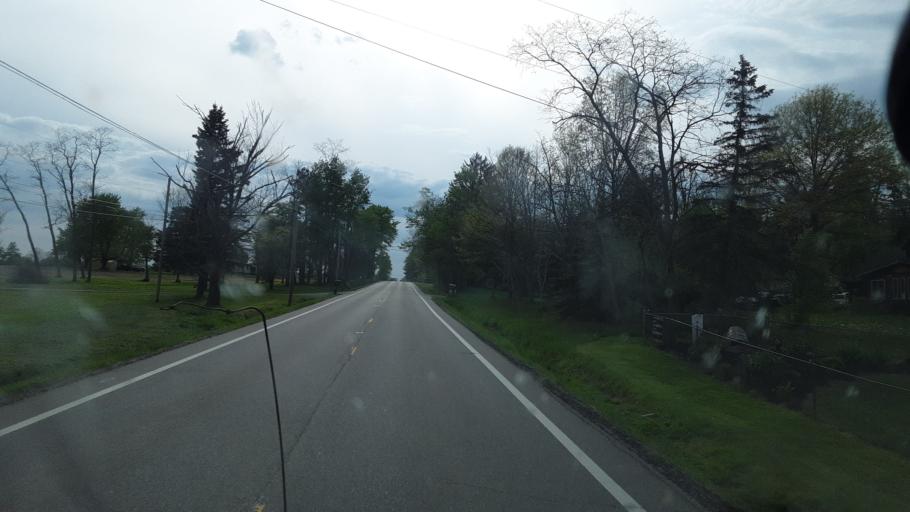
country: US
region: Ohio
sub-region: Portage County
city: Garrettsville
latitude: 41.2352
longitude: -81.1095
